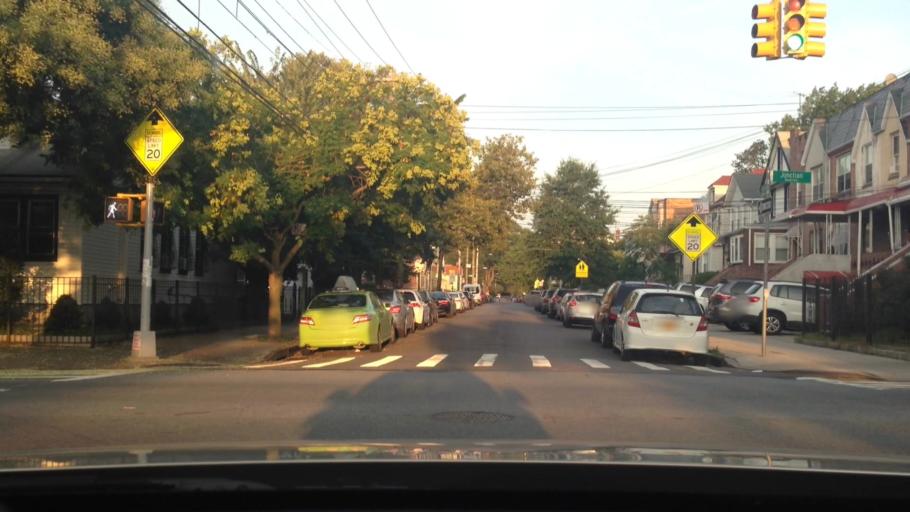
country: US
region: New York
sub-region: Queens County
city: Borough of Queens
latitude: 40.7382
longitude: -73.8664
